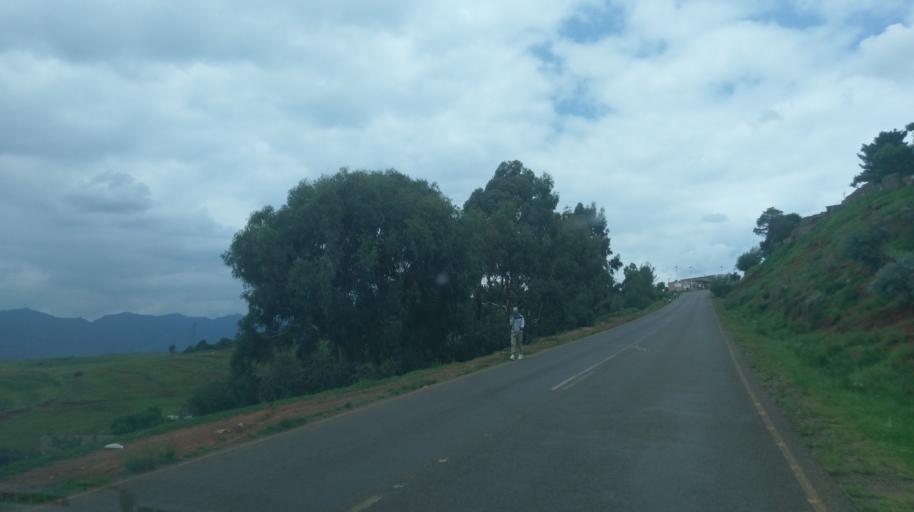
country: LS
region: Leribe
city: Leribe
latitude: -28.9992
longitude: 28.2065
